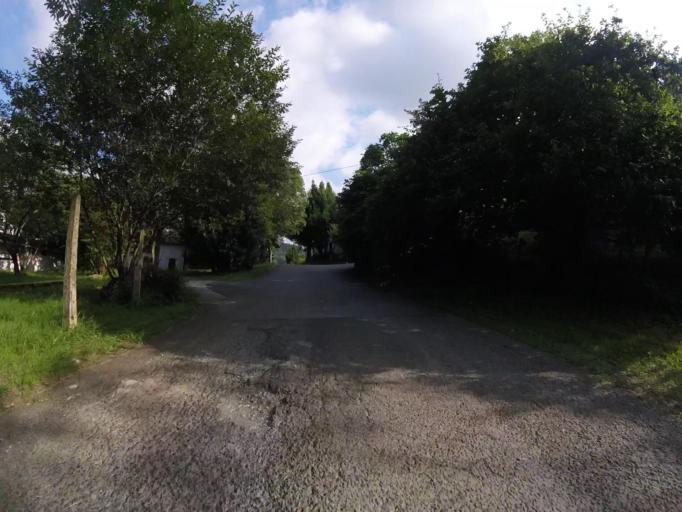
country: ES
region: Basque Country
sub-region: Provincia de Guipuzcoa
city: Astigarraga
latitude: 43.2571
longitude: -1.9503
